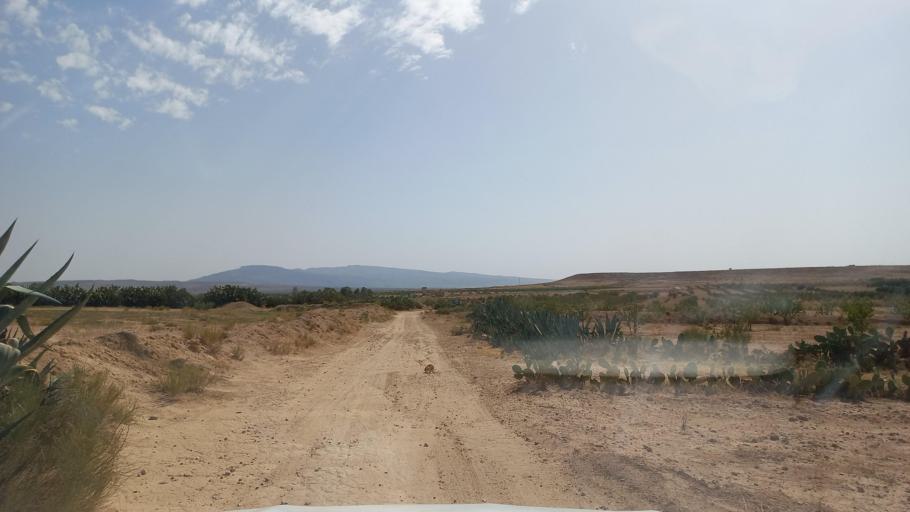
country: TN
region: Al Qasrayn
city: Kasserine
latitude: 35.2769
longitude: 8.9696
